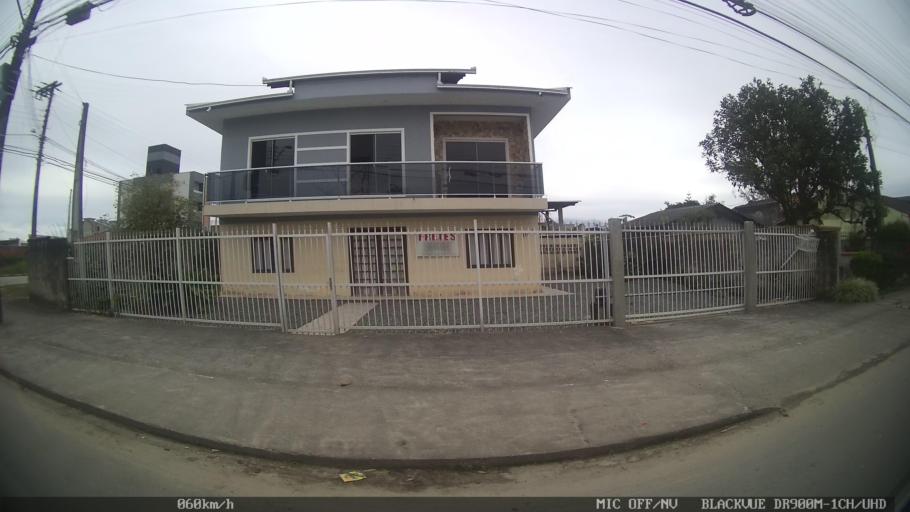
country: BR
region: Santa Catarina
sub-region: Joinville
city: Joinville
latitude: -26.2983
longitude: -48.8998
